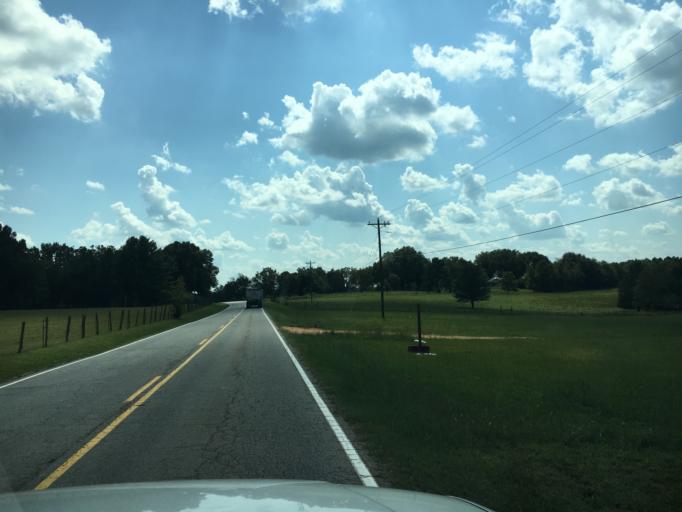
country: US
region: South Carolina
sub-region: Spartanburg County
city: Woodruff
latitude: 34.7106
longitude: -82.0476
